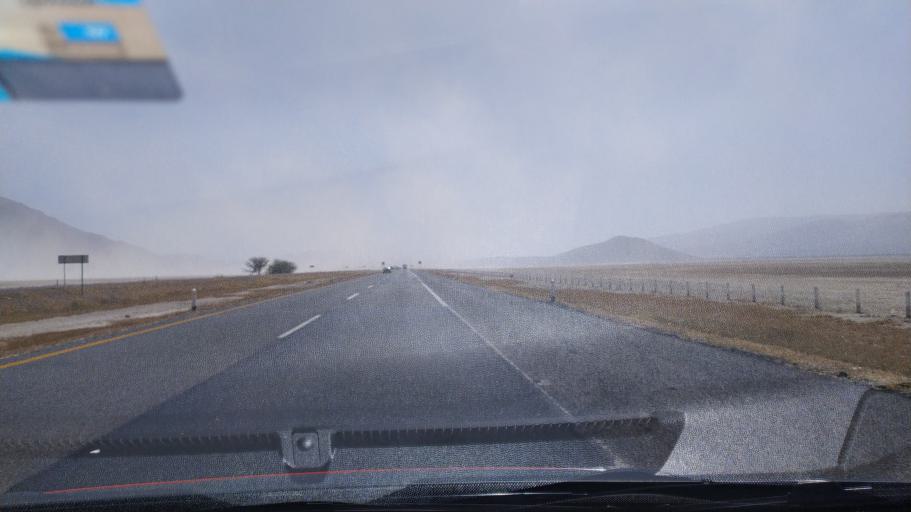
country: MX
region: Jalisco
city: Zacoalco de Torres
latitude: 20.3144
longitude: -103.5634
